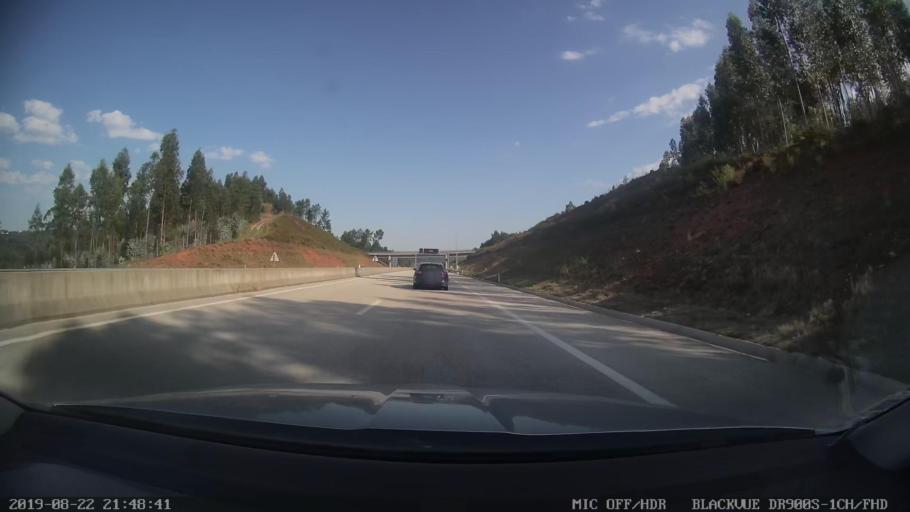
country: PT
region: Coimbra
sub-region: Penela
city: Penela
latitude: 40.0302
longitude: -8.3694
